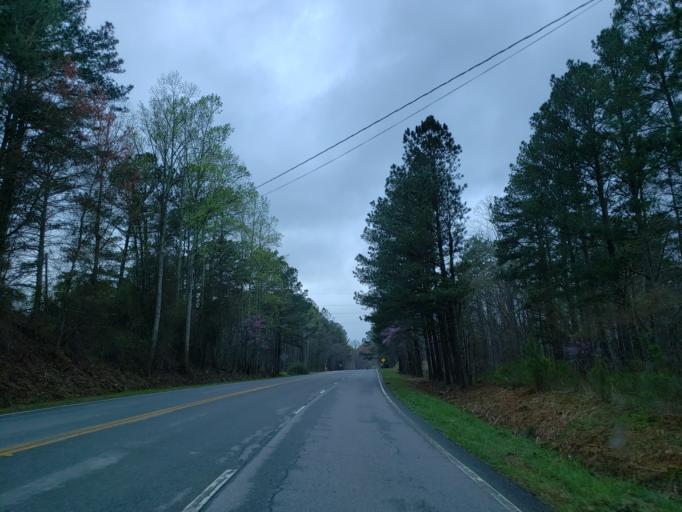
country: US
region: Georgia
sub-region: Polk County
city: Rockmart
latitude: 33.9217
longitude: -84.9668
